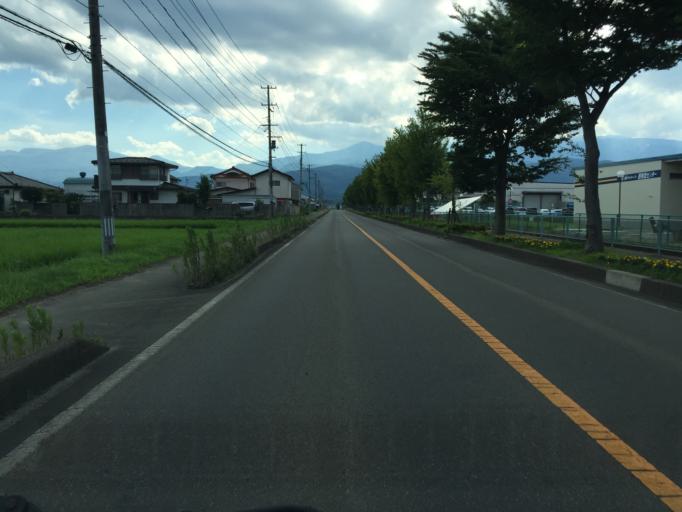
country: JP
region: Fukushima
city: Fukushima-shi
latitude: 37.7462
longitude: 140.3956
